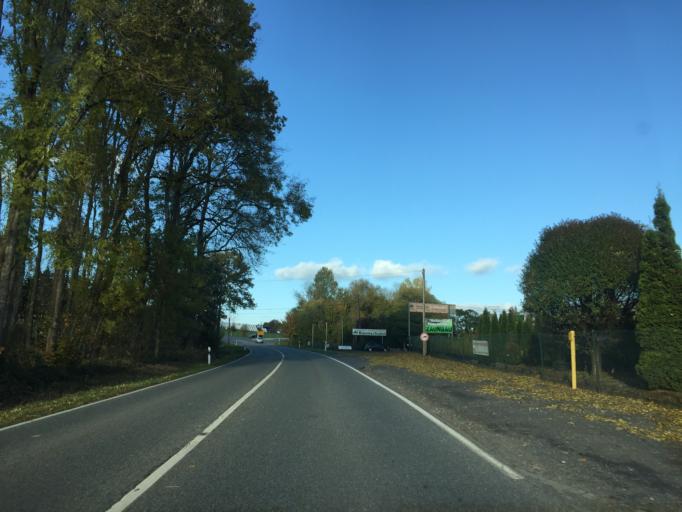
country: DE
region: Rheinland-Pfalz
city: Dreikirchen
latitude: 50.4490
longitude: 7.9437
